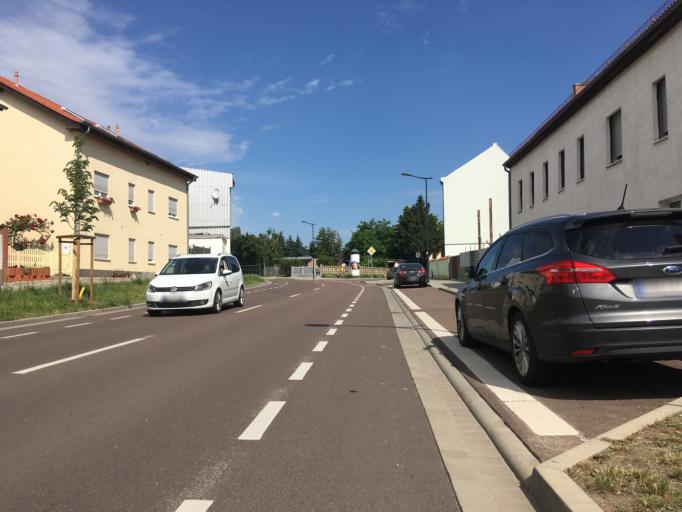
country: DE
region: Saxony-Anhalt
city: Bernburg
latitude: 51.7810
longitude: 11.7667
